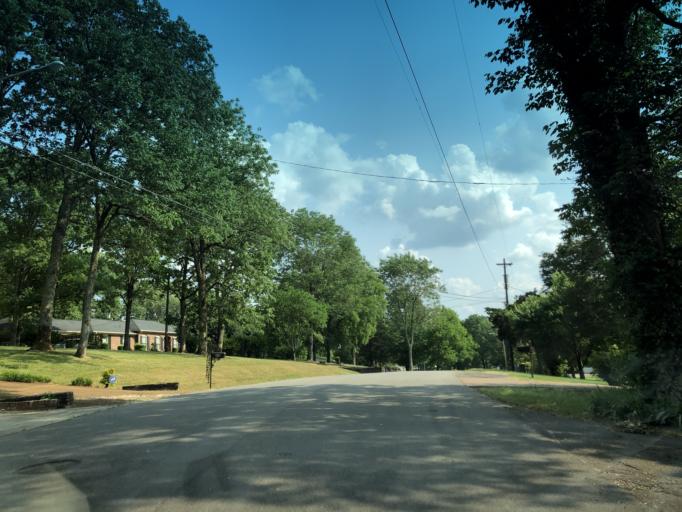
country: US
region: Tennessee
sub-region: Davidson County
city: Goodlettsville
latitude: 36.2748
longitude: -86.7315
